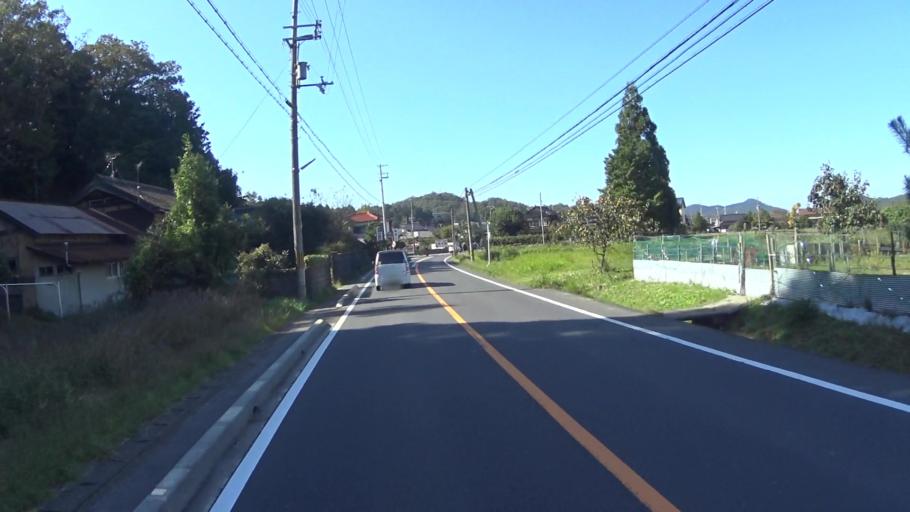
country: JP
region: Hyogo
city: Toyooka
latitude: 35.5809
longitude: 134.9648
